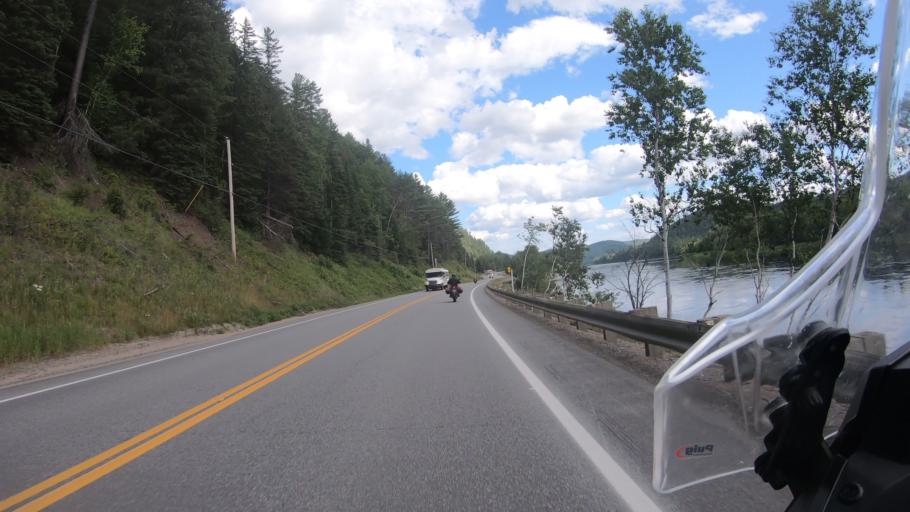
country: CA
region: Quebec
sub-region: Mauricie
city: Saint-Tite
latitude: 46.9952
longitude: -72.9180
